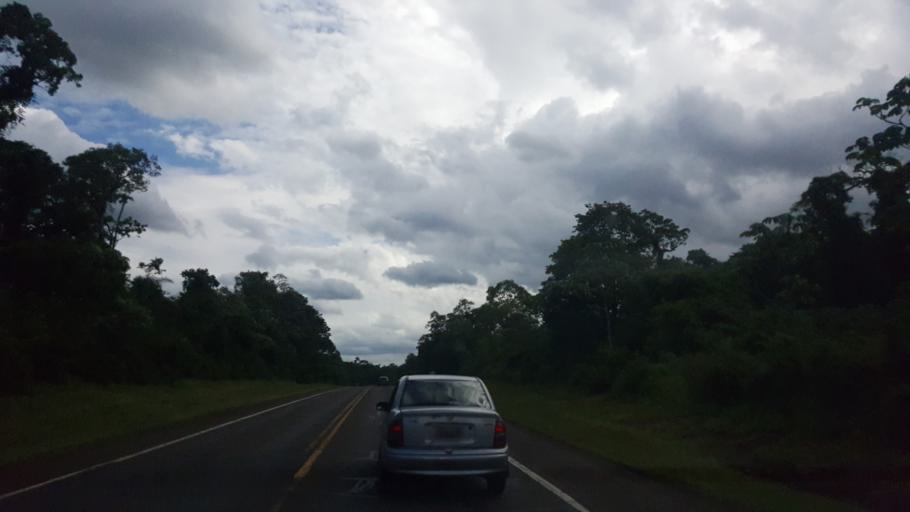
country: AR
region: Misiones
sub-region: Departamento de Iguazu
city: Puerto Iguazu
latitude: -25.7138
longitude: -54.5190
